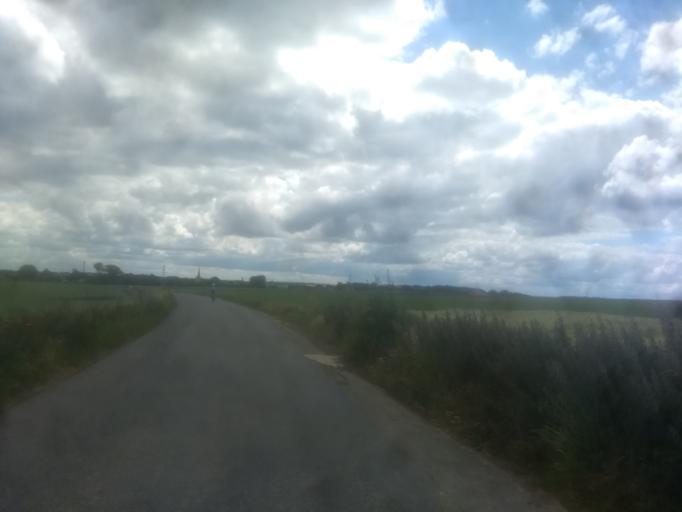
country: FR
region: Nord-Pas-de-Calais
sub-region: Departement du Pas-de-Calais
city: Agny
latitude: 50.2322
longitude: 2.7327
